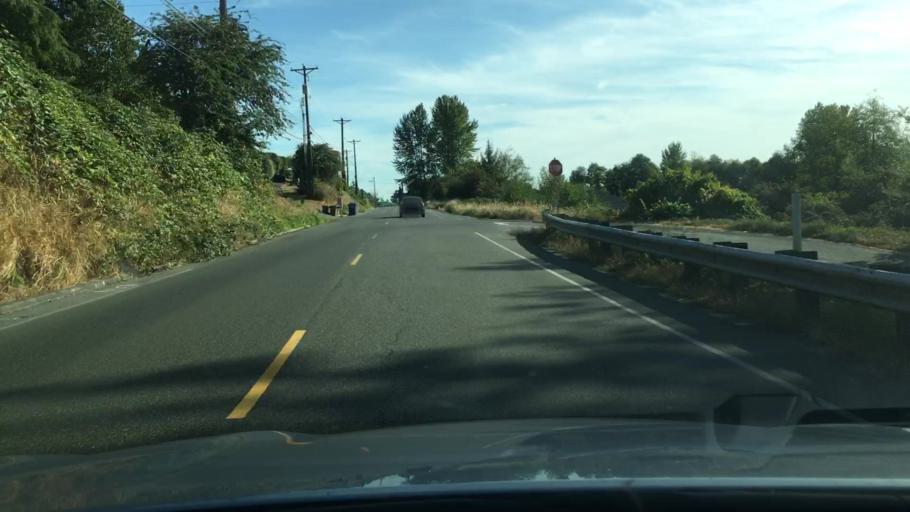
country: US
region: Washington
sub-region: Pierce County
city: Tacoma
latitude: 47.3052
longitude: -122.4343
